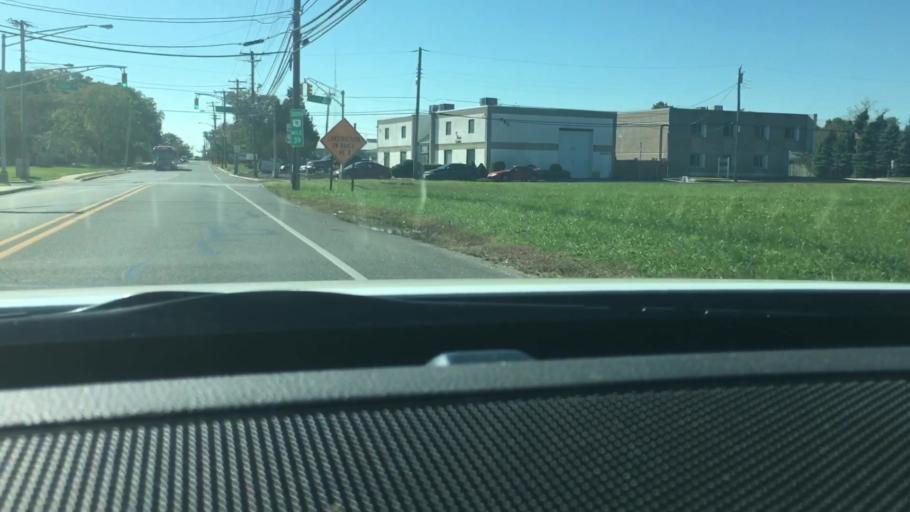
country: US
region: New Jersey
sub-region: Atlantic County
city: Northfield
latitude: 39.3838
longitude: -74.5421
